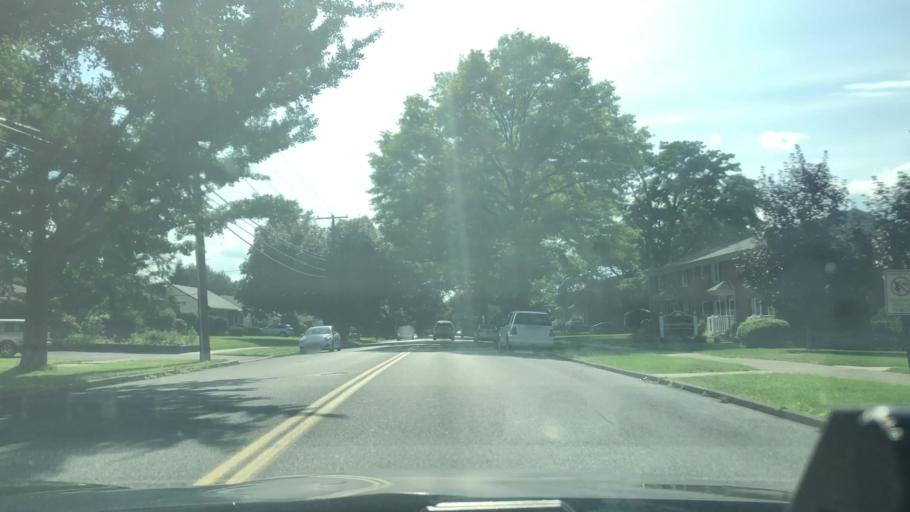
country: US
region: Pennsylvania
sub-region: Northampton County
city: Bethlehem
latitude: 40.6399
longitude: -75.4024
